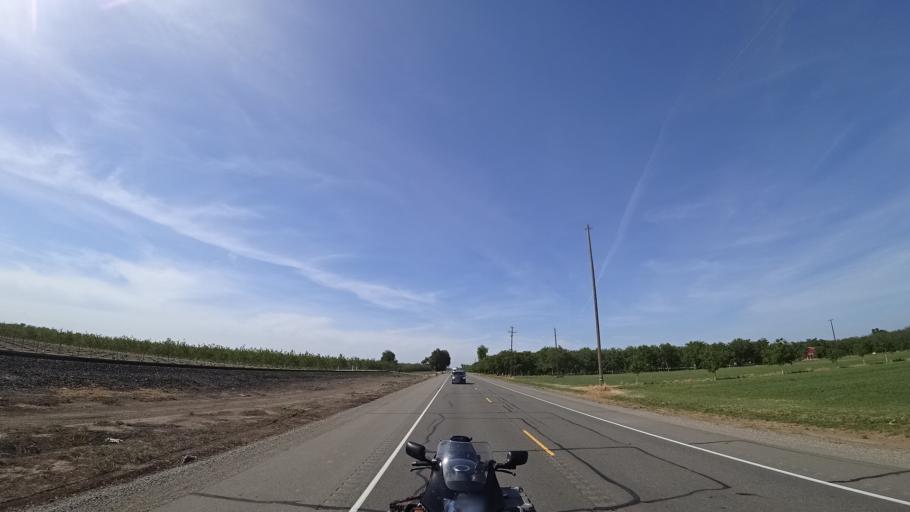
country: US
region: California
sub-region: Tehama County
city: Los Molinos
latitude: 39.9870
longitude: -122.0826
